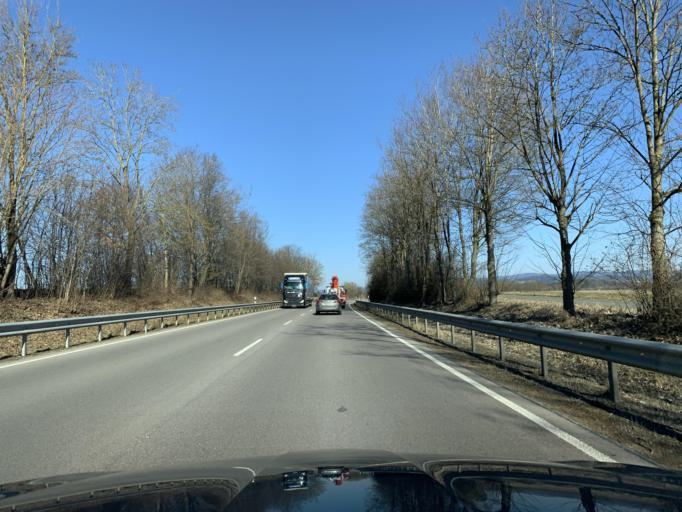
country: DE
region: Bavaria
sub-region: Upper Palatinate
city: Schonthal
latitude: 49.3497
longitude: 12.5865
